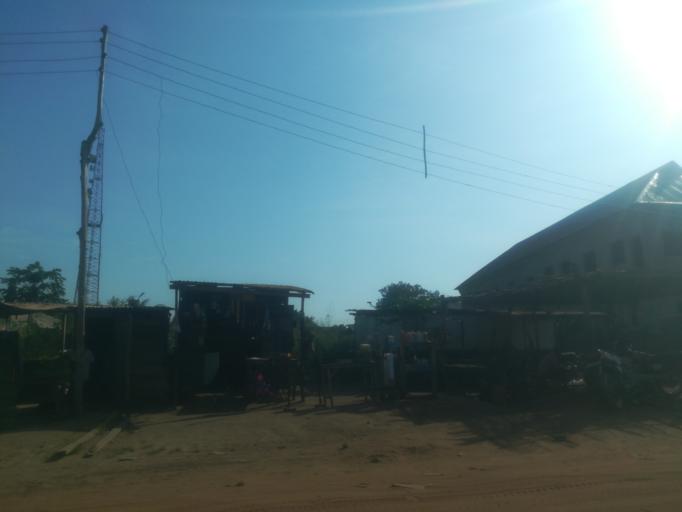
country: NG
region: Ogun
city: Abeokuta
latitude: 7.1404
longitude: 3.2648
